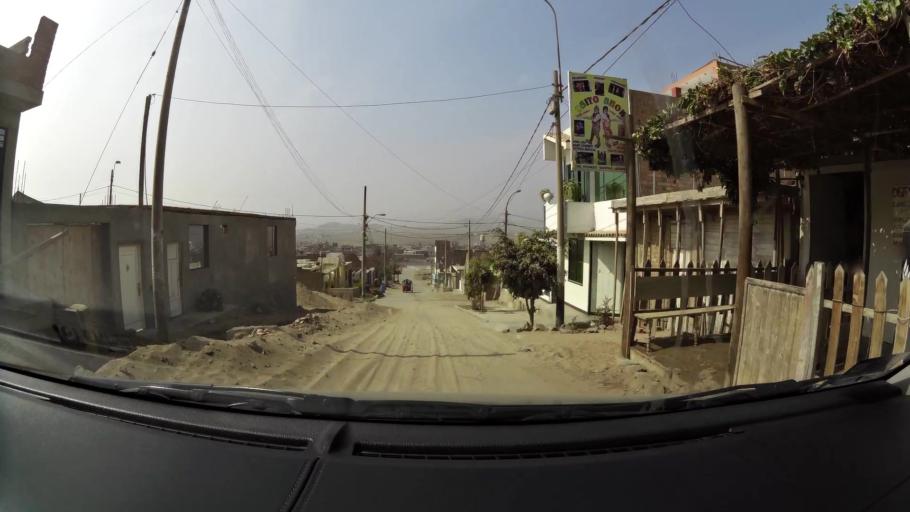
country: PE
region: Lima
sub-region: Lima
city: Santa Rosa
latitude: -11.7858
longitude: -77.1621
